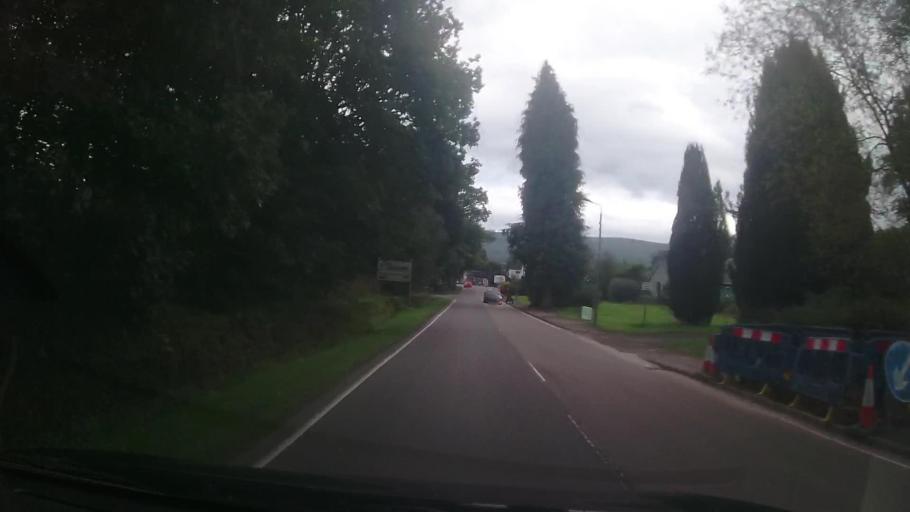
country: GB
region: Scotland
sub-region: Argyll and Bute
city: Garelochhead
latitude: 56.2323
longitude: -5.0770
